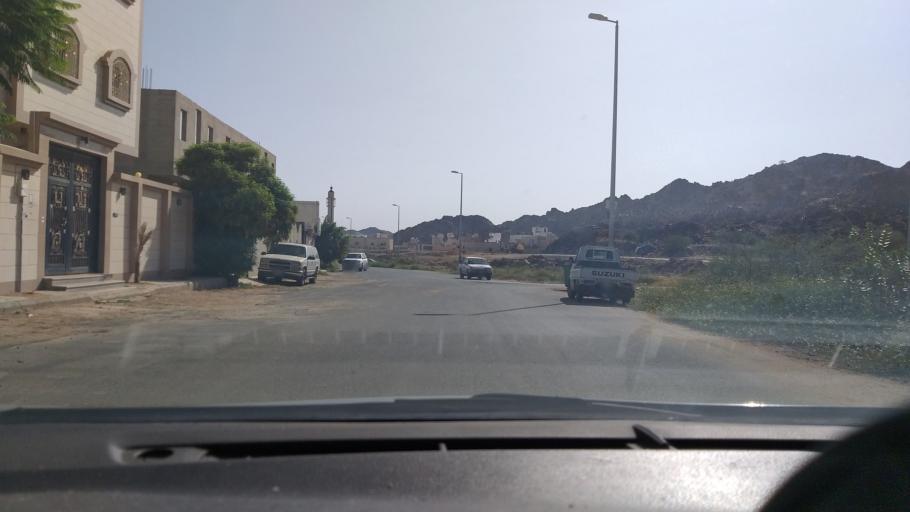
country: SA
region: Makkah
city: Ta'if
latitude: 21.2216
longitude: 40.3705
